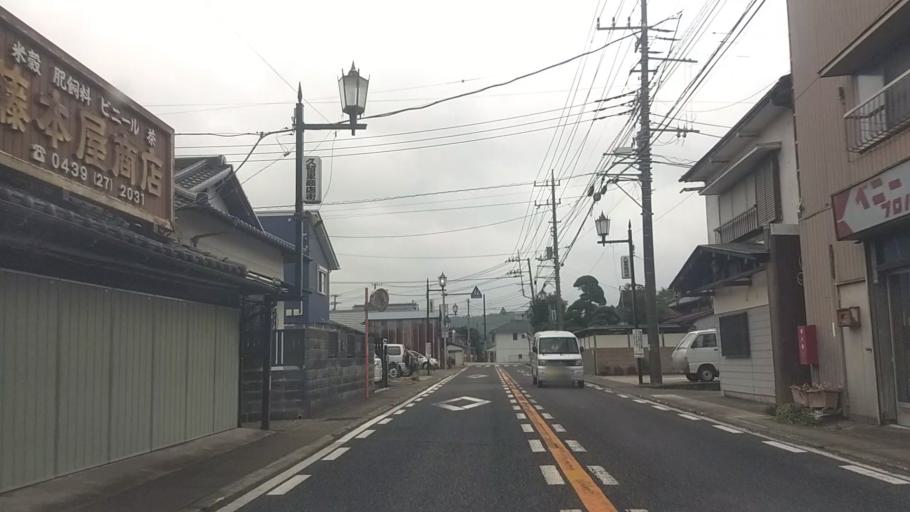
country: JP
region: Chiba
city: Kisarazu
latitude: 35.2943
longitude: 140.0785
